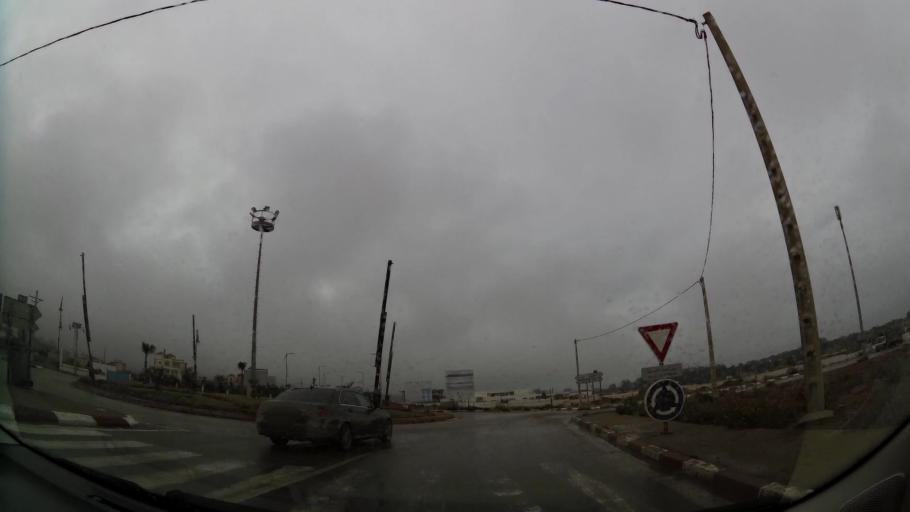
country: MA
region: Taza-Al Hoceima-Taounate
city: Imzourene
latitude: 35.1963
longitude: -3.8945
